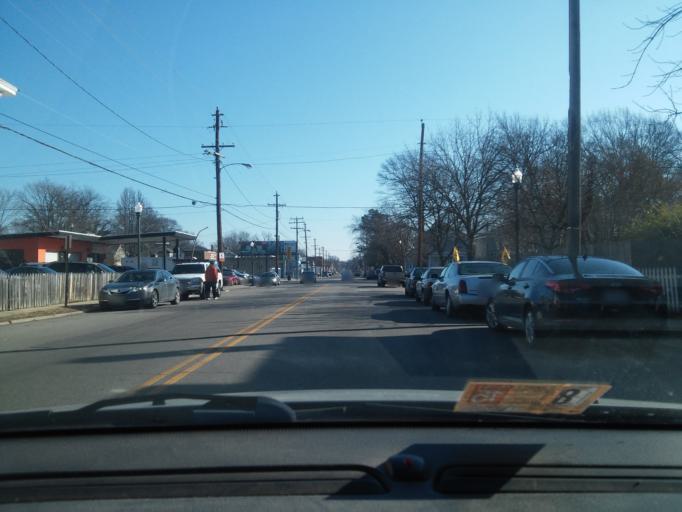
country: US
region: Virginia
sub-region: City of Richmond
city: Richmond
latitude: 37.5718
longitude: -77.4397
